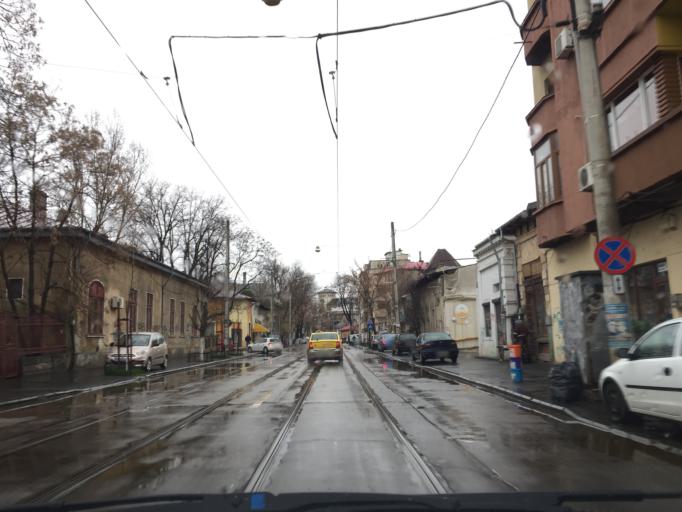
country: RO
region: Bucuresti
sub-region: Municipiul Bucuresti
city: Bucuresti
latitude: 44.4204
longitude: 26.0954
